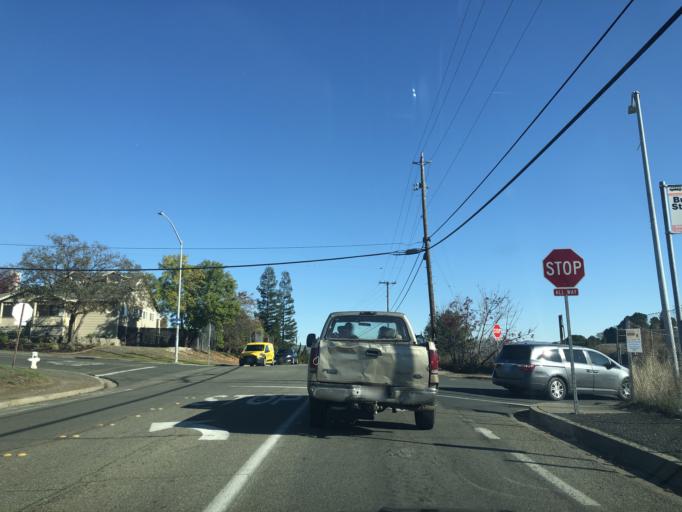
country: US
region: California
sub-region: Contra Costa County
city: Pacheco
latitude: 37.9917
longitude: -122.0868
